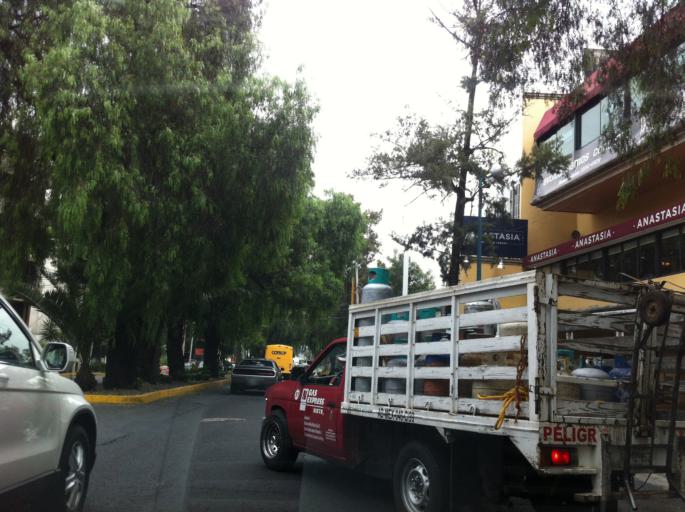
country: MX
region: Mexico City
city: Alvaro Obregon
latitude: 19.3493
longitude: -99.1899
